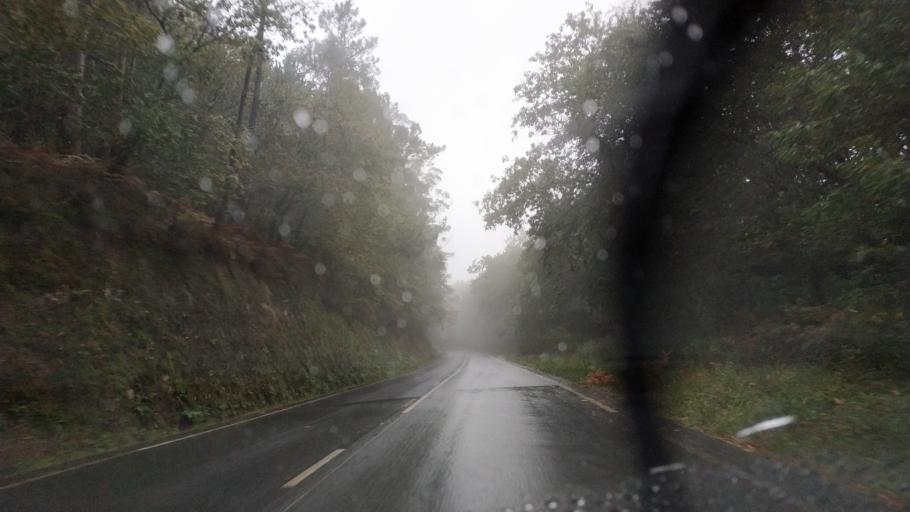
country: ES
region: Galicia
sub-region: Provincia da Coruna
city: Negreira
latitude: 42.9101
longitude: -8.7504
